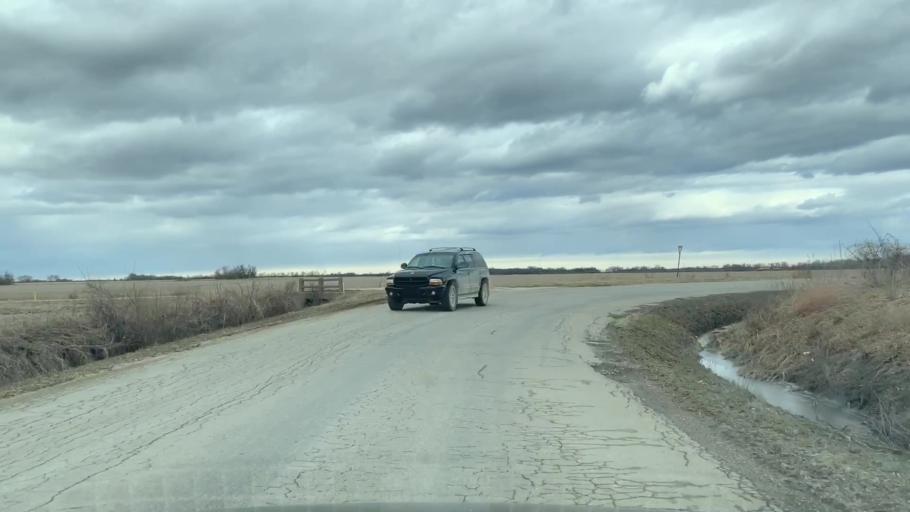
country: US
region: Kansas
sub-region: Allen County
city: Humboldt
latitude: 37.8125
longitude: -95.4705
